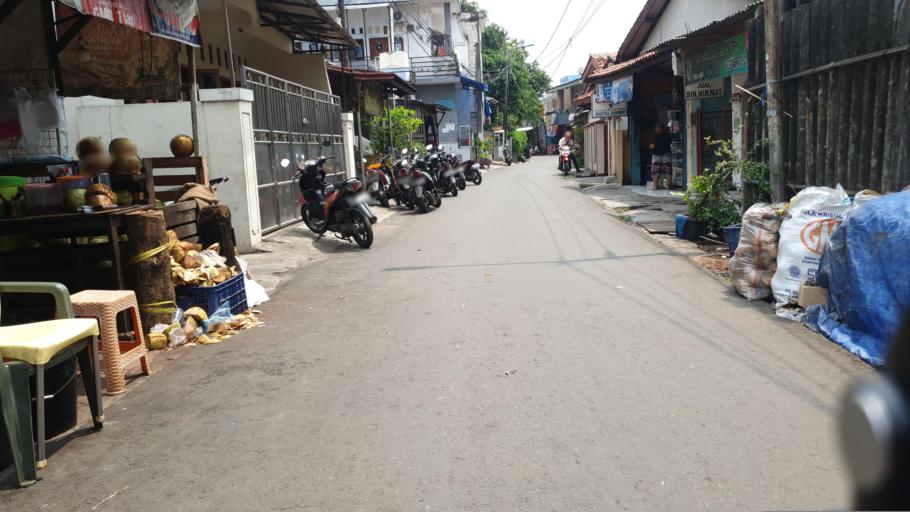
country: ID
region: West Java
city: Ciputat
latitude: -6.1951
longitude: 106.7521
